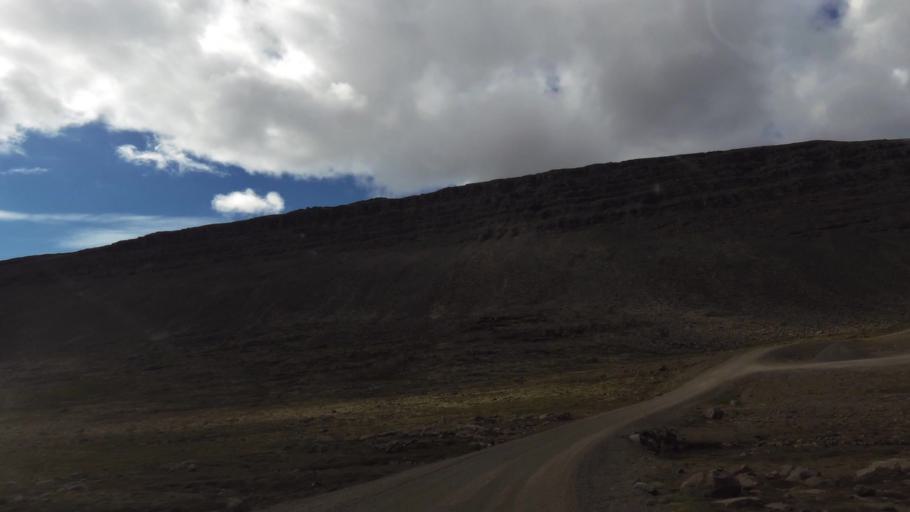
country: IS
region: West
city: Olafsvik
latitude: 65.5757
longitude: -24.0828
